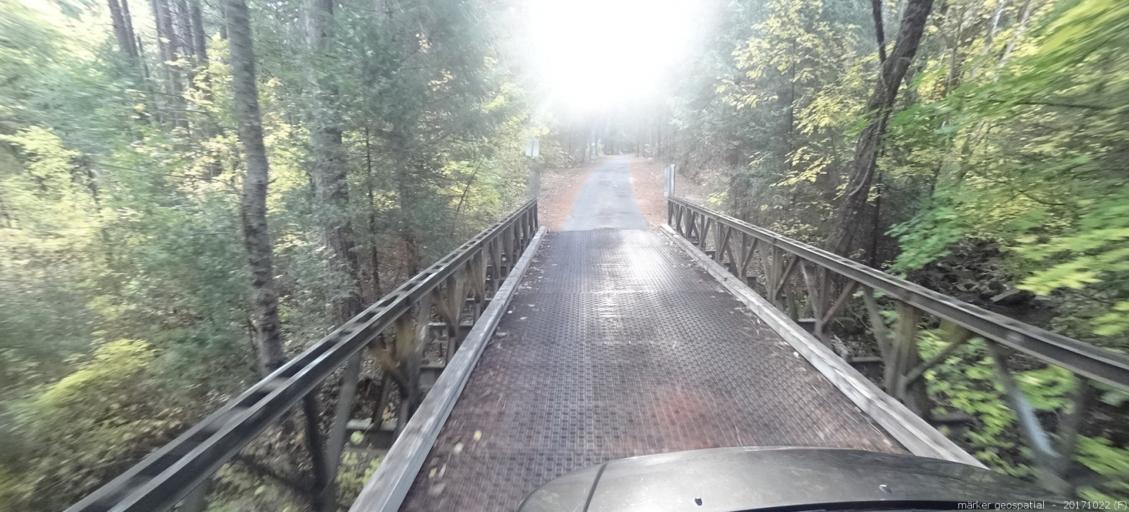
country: US
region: California
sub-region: Siskiyou County
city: Dunsmuir
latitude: 41.1713
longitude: -122.2732
